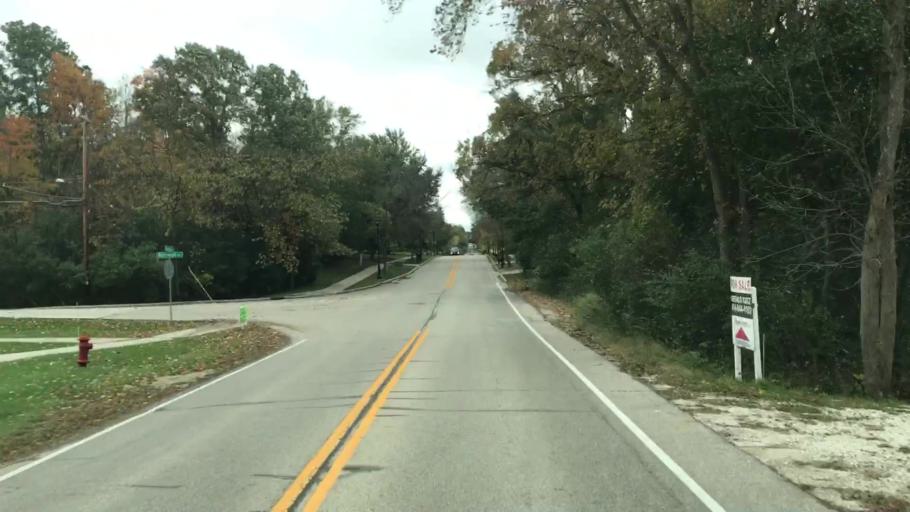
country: US
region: Wisconsin
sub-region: Waukesha County
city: Brookfield
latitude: 43.0763
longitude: -88.1459
